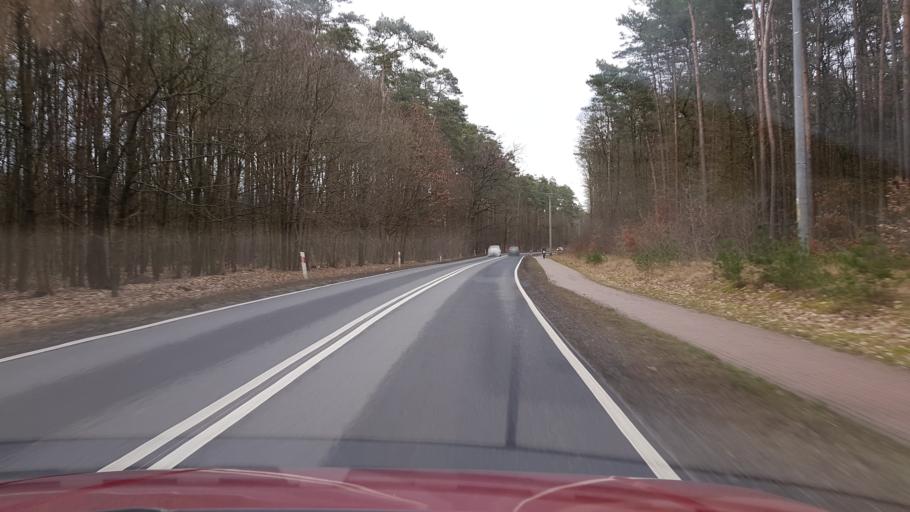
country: PL
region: West Pomeranian Voivodeship
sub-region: Powiat policki
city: Police
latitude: 53.5427
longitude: 14.4869
